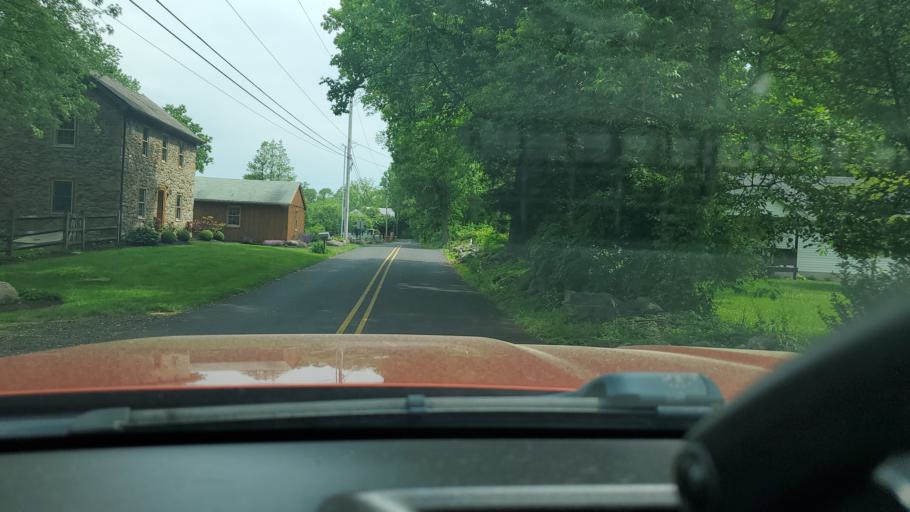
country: US
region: Pennsylvania
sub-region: Montgomery County
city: Red Hill
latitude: 40.3310
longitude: -75.5149
